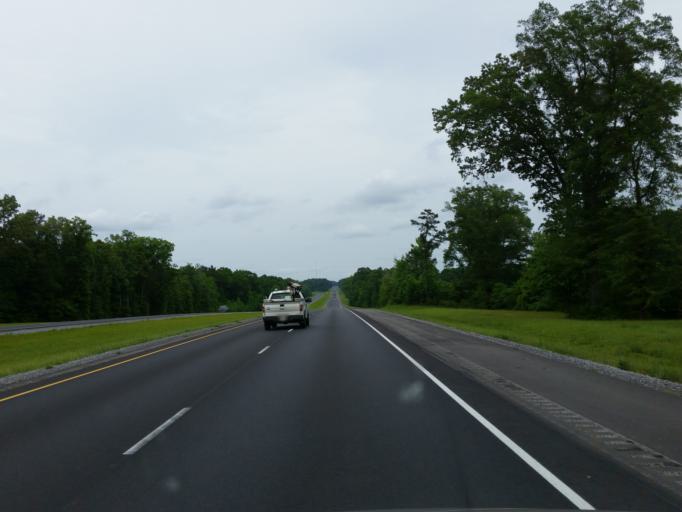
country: US
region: Mississippi
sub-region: Jones County
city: Sharon
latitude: 31.9332
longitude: -88.9956
